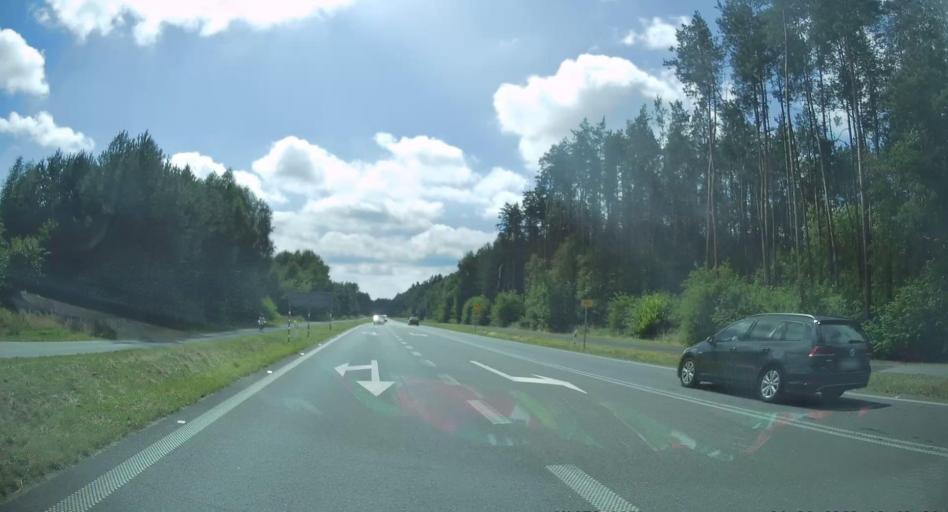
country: PL
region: Subcarpathian Voivodeship
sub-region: Powiat mielecki
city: Padew Narodowa
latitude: 50.3659
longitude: 21.4830
